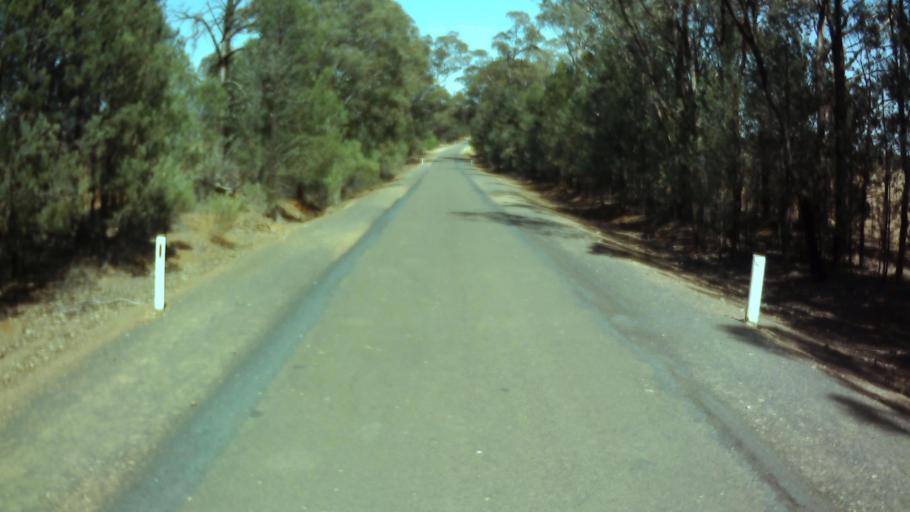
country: AU
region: New South Wales
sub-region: Weddin
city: Grenfell
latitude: -33.8706
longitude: 148.0947
